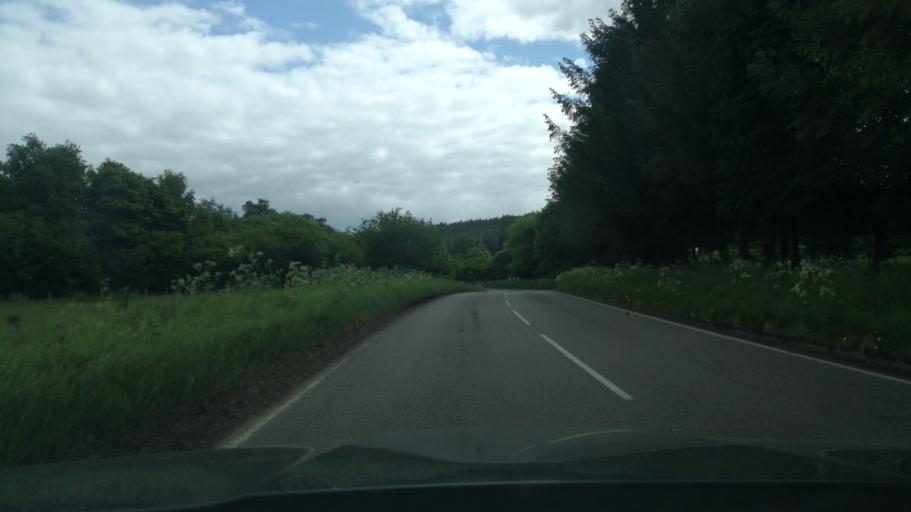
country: GB
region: Scotland
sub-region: Moray
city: Fochabers
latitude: 57.5465
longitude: -3.1198
